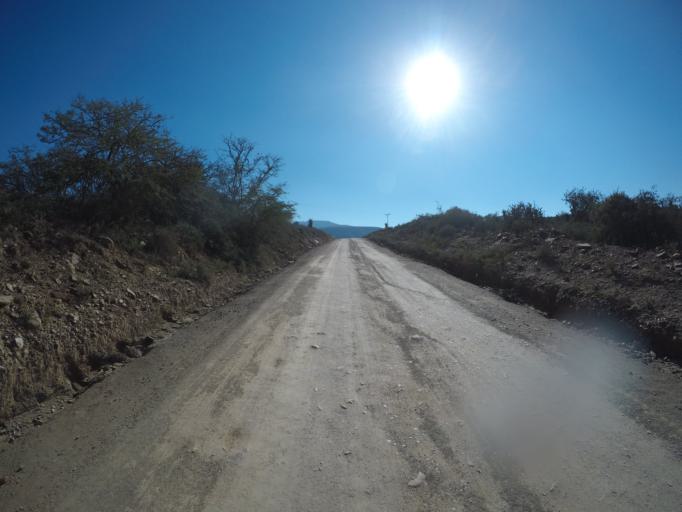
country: ZA
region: Eastern Cape
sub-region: Cacadu District Municipality
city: Kruisfontein
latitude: -33.6728
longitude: 24.5764
